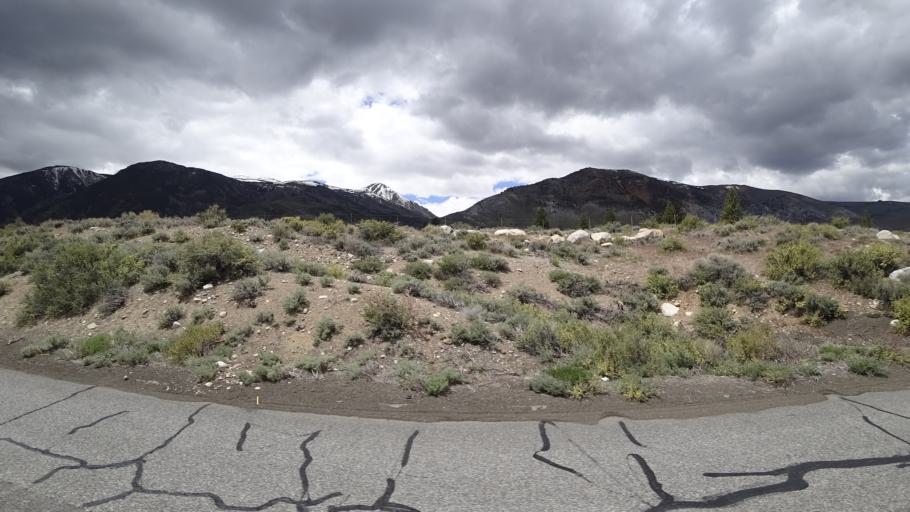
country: US
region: California
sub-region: Mono County
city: Bridgeport
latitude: 38.0386
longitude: -119.1583
